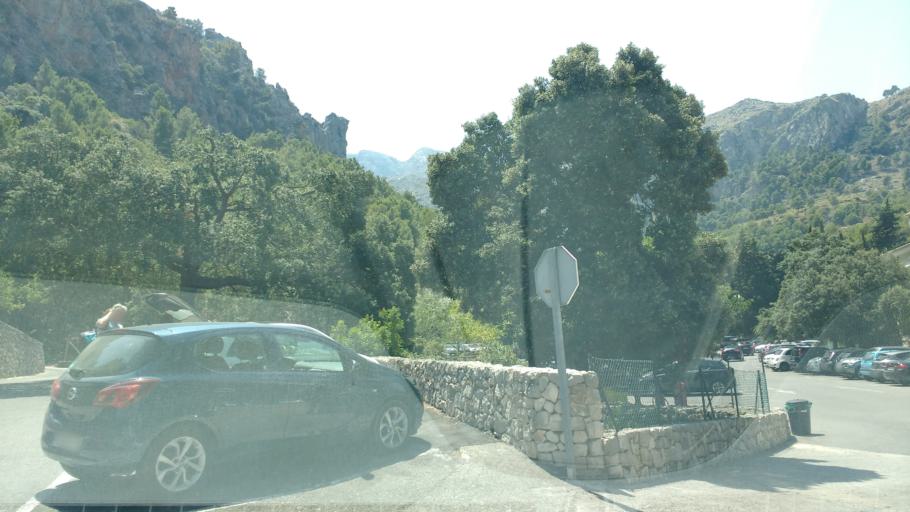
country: ES
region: Balearic Islands
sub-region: Illes Balears
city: Escorca
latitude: 39.8478
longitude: 2.7986
